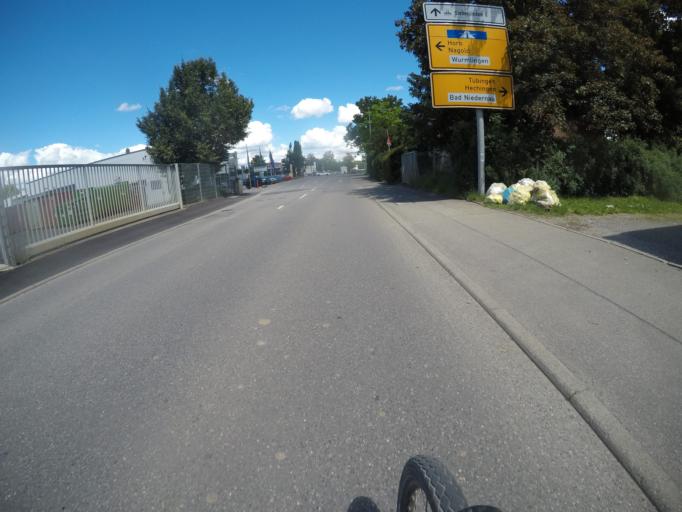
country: DE
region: Baden-Wuerttemberg
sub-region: Tuebingen Region
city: Rottenburg
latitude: 48.4754
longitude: 8.9543
